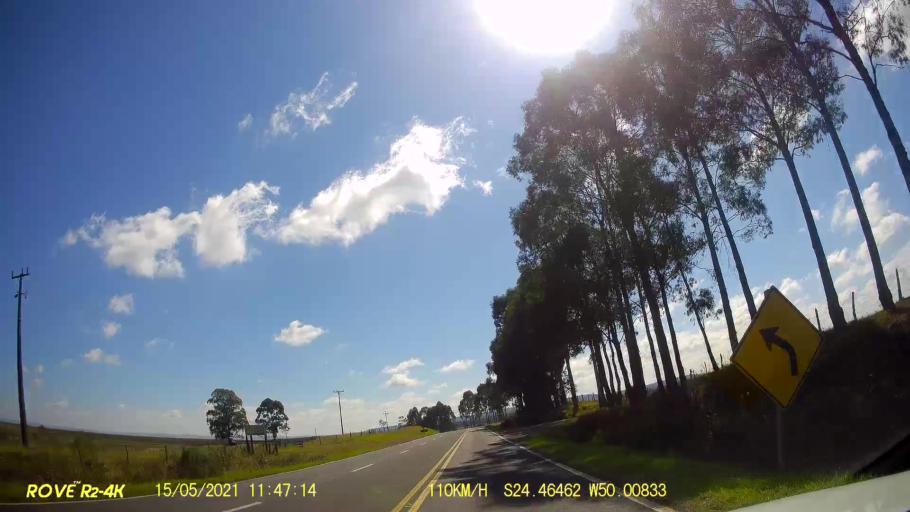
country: BR
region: Parana
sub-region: Pirai Do Sul
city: Pirai do Sul
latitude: -24.4647
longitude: -50.0083
